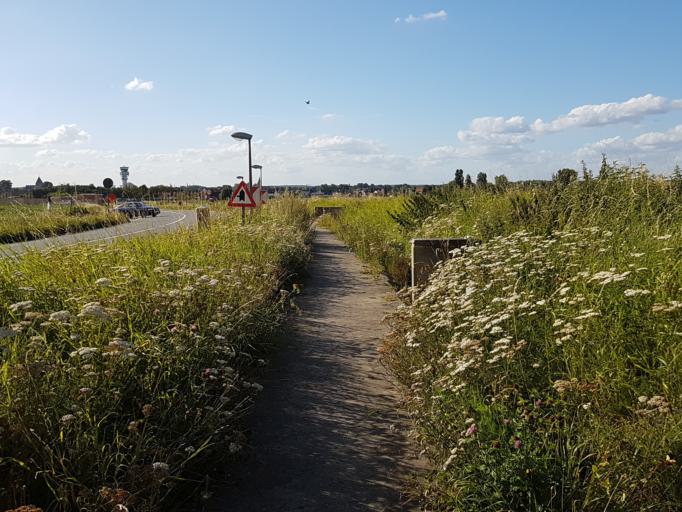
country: BE
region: Flanders
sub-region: Provincie Vlaams-Brabant
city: Kortenberg
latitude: 50.8986
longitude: 4.5301
